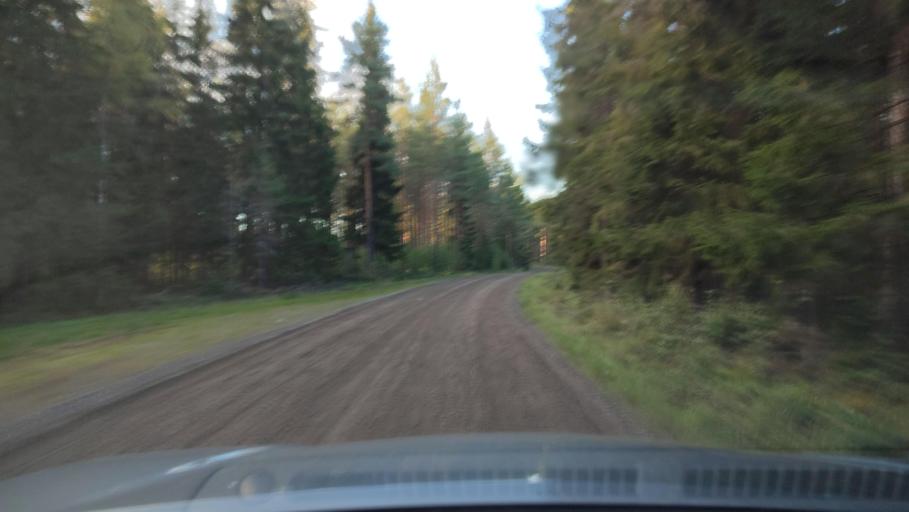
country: FI
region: Southern Ostrobothnia
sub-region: Suupohja
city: Karijoki
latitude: 62.2293
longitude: 21.5730
